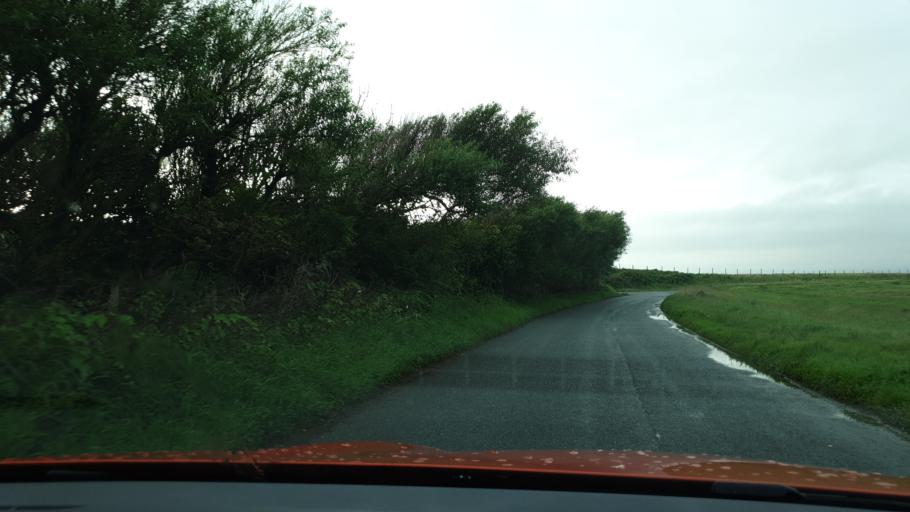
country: GB
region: England
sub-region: Cumbria
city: Barrow in Furness
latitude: 54.0666
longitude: -3.2245
